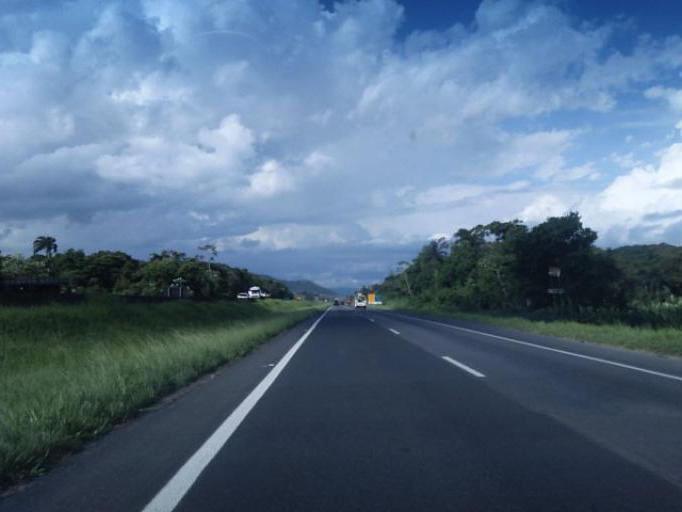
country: BR
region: Sao Paulo
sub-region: Juquia
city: Juquia
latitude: -24.3462
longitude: -47.6491
